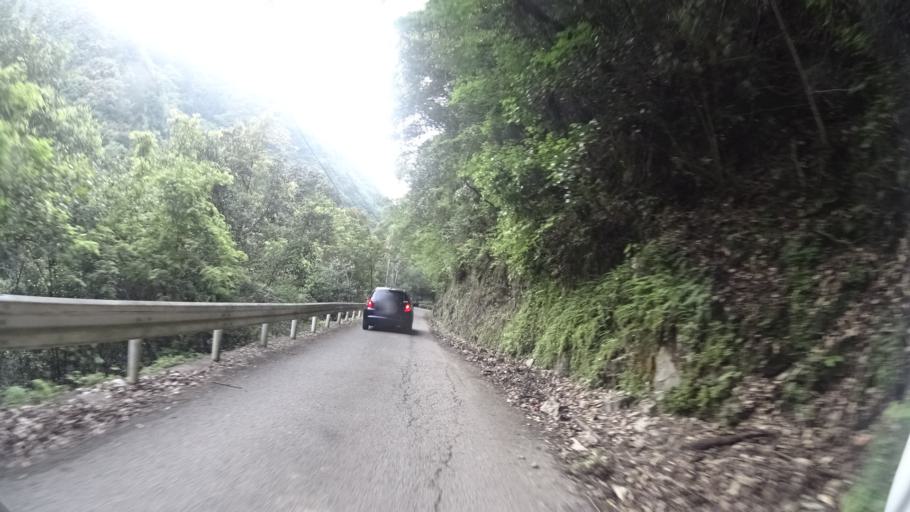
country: JP
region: Tokushima
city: Ikedacho
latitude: 33.9410
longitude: 133.8084
